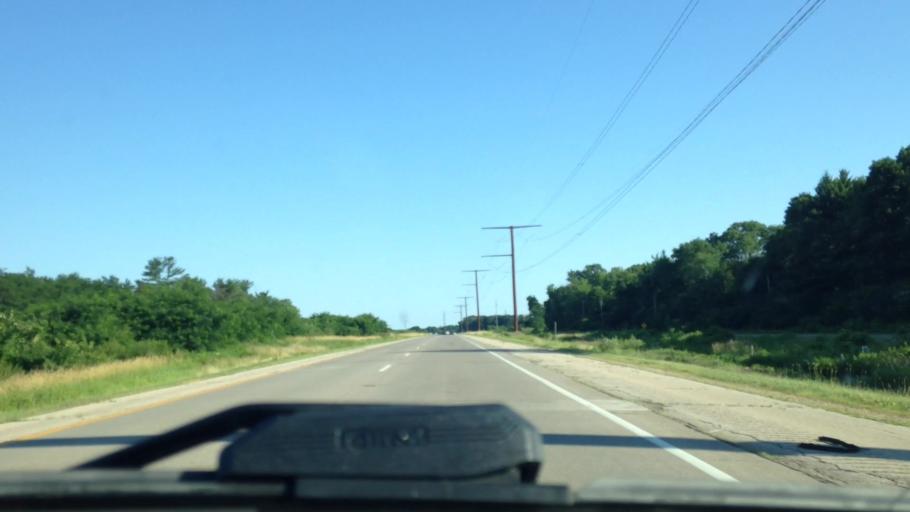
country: US
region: Wisconsin
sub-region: Juneau County
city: Mauston
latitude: 43.8336
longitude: -90.0903
